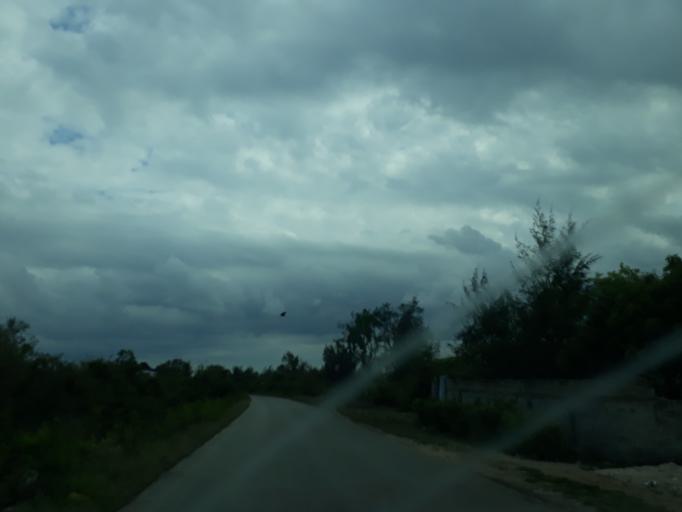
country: TZ
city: Kiwengwa
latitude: -6.0847
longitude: 39.4249
